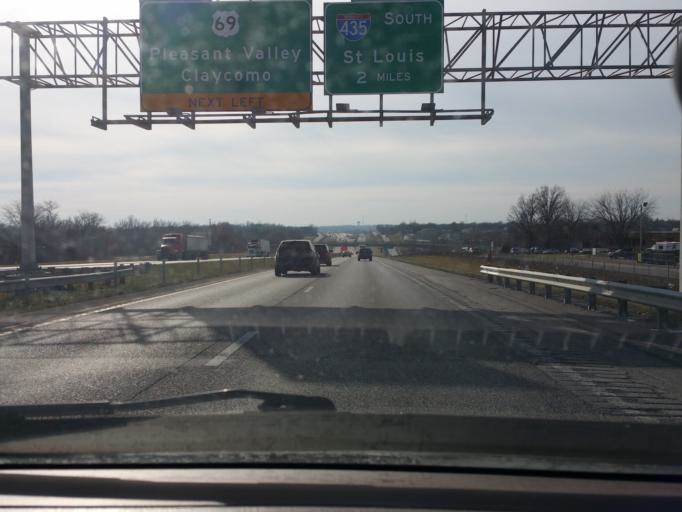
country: US
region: Missouri
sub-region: Clay County
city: Pleasant Valley
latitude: 39.2326
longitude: -94.4644
